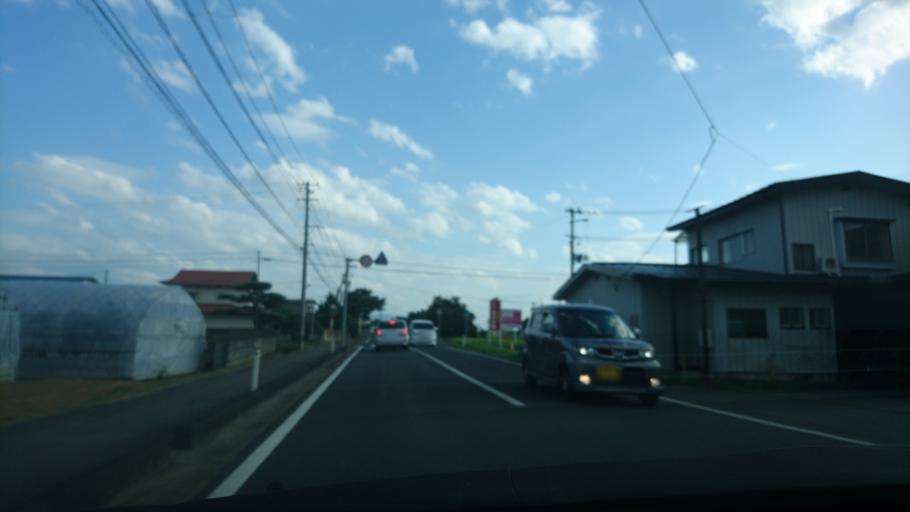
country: JP
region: Iwate
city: Mizusawa
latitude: 39.1571
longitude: 141.1803
